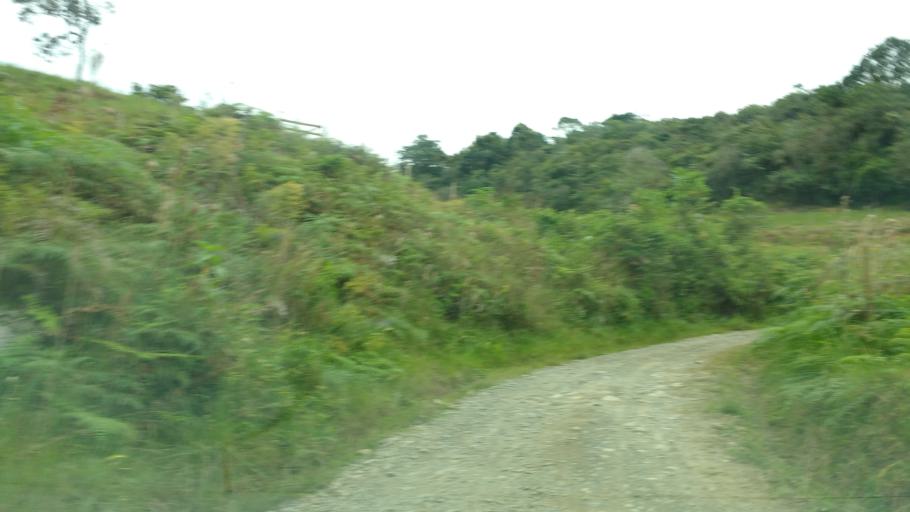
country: CO
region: Antioquia
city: Concepcion
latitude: 6.3705
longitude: -75.2299
